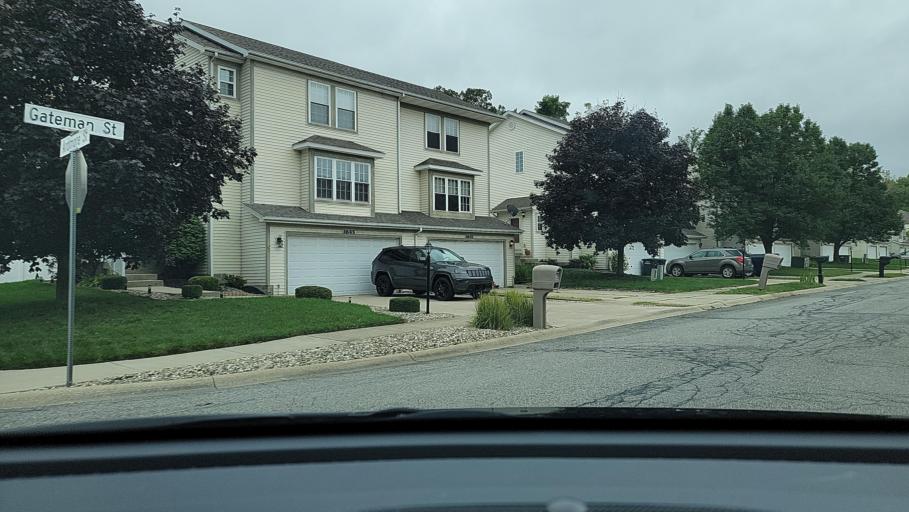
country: US
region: Indiana
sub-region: Porter County
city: Portage
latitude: 41.5464
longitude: -87.1953
